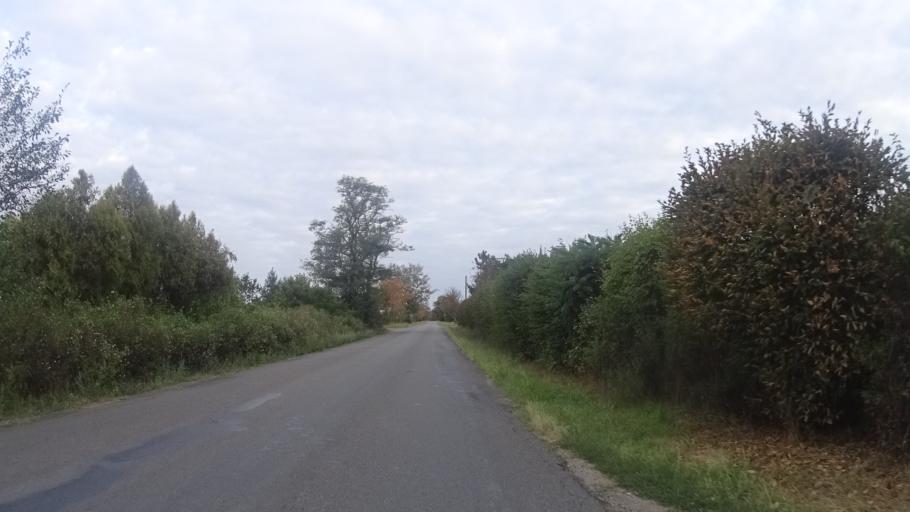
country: CZ
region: Kralovehradecky
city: Cernilov
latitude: 50.2093
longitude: 15.9182
